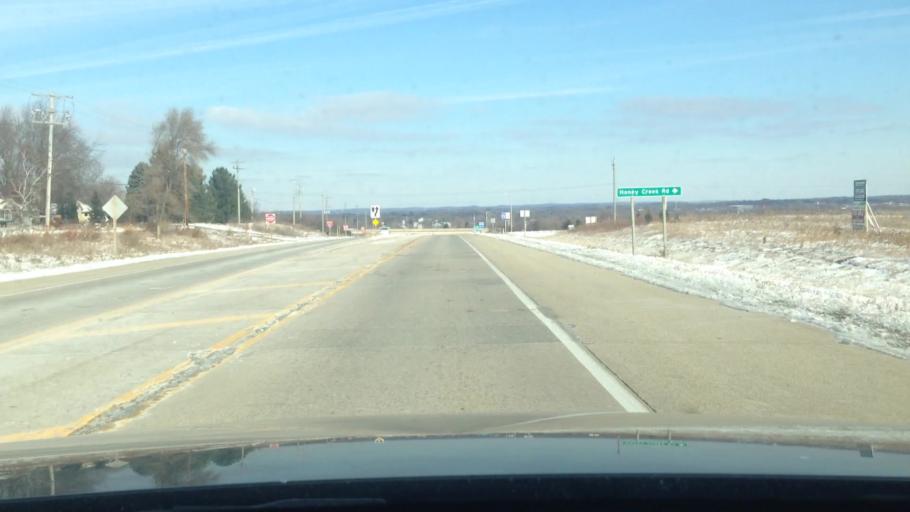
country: US
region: Wisconsin
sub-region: Walworth County
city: East Troy
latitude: 42.7689
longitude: -88.4063
